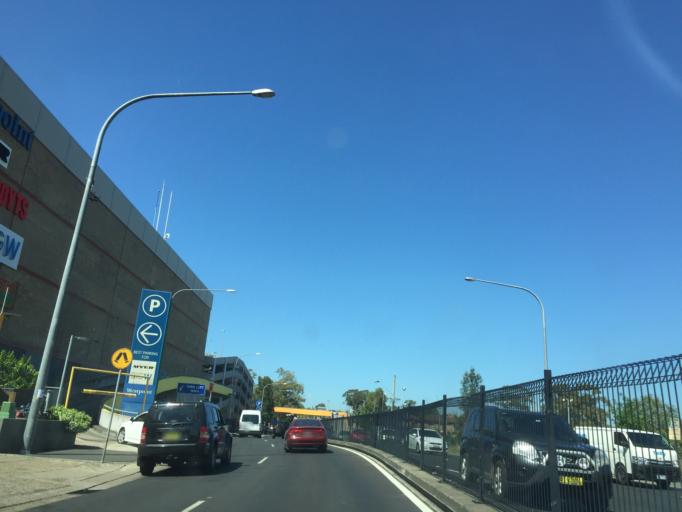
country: AU
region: New South Wales
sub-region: Blacktown
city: Blacktown
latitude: -33.7691
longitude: 150.9043
